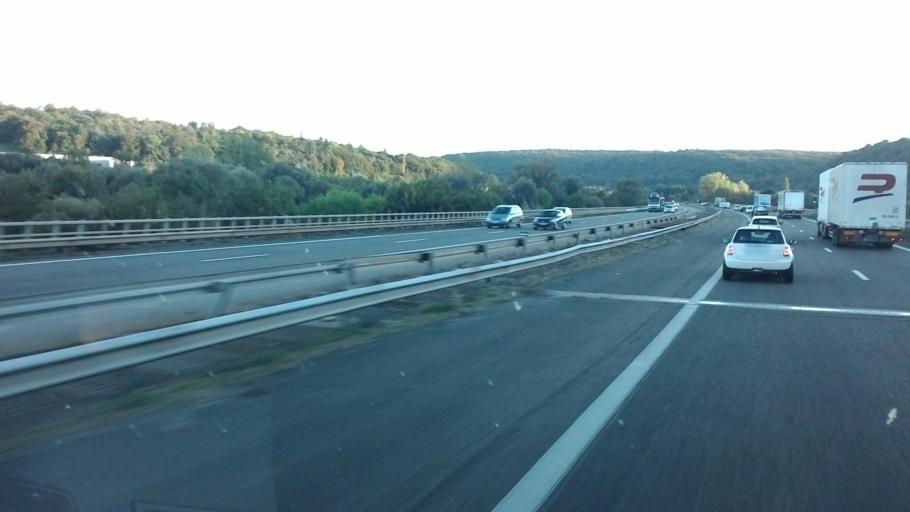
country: FR
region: Lorraine
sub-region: Departement de Meurthe-et-Moselle
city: Belleville
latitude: 48.8063
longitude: 6.1133
